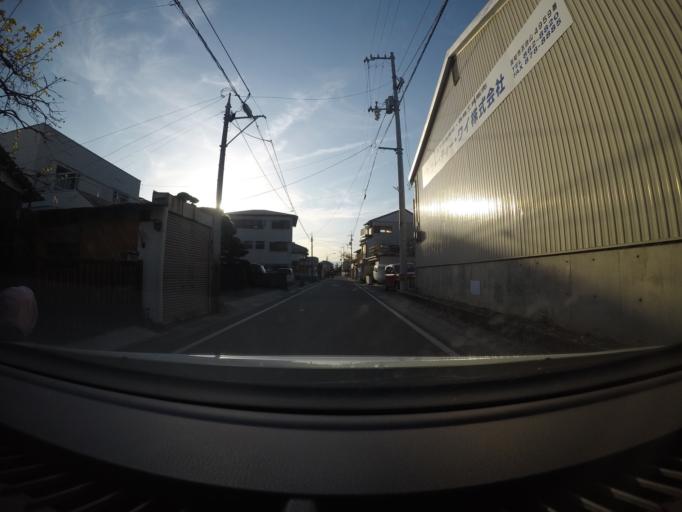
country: JP
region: Kochi
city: Kochi-shi
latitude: 33.5435
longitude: 133.5723
